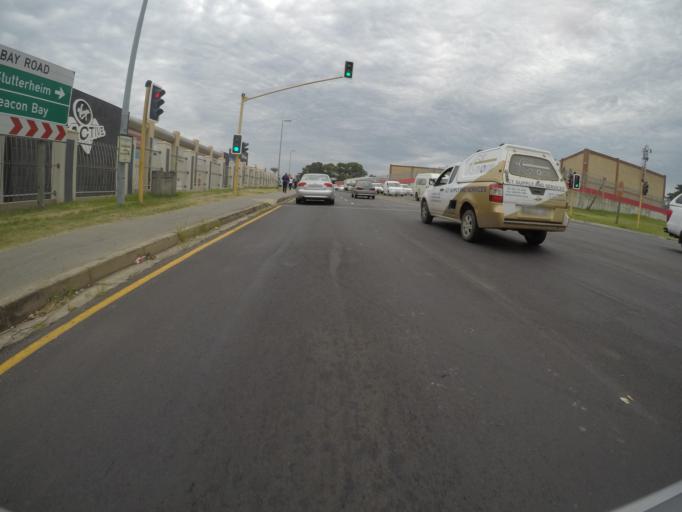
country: ZA
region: Eastern Cape
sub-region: Buffalo City Metropolitan Municipality
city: East London
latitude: -32.9516
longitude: 27.9307
